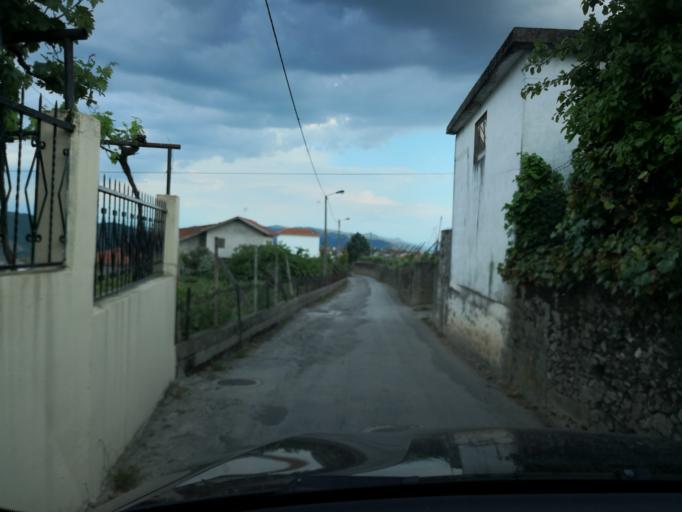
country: PT
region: Vila Real
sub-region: Sabrosa
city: Vilela
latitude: 41.2077
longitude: -7.6598
